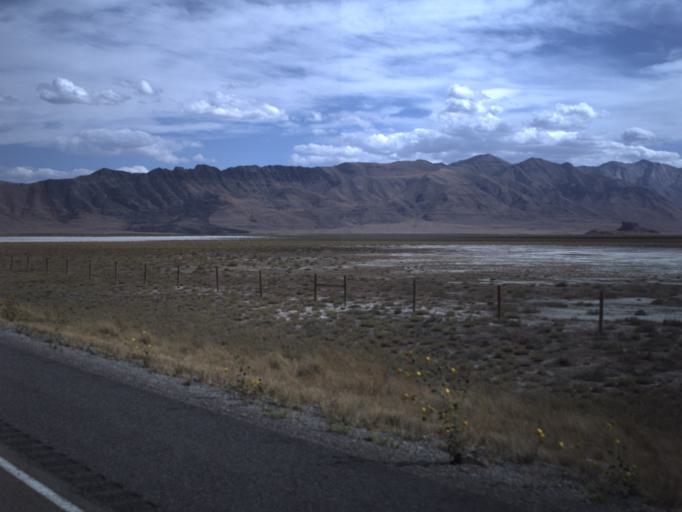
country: US
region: Utah
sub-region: Tooele County
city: Grantsville
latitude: 40.7517
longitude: -112.7137
